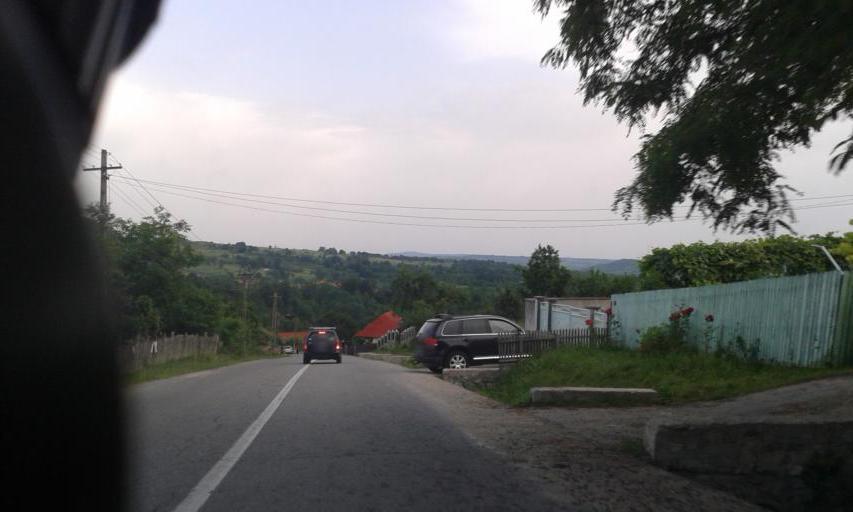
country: RO
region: Gorj
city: Novaci-Straini
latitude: 45.1841
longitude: 23.6815
